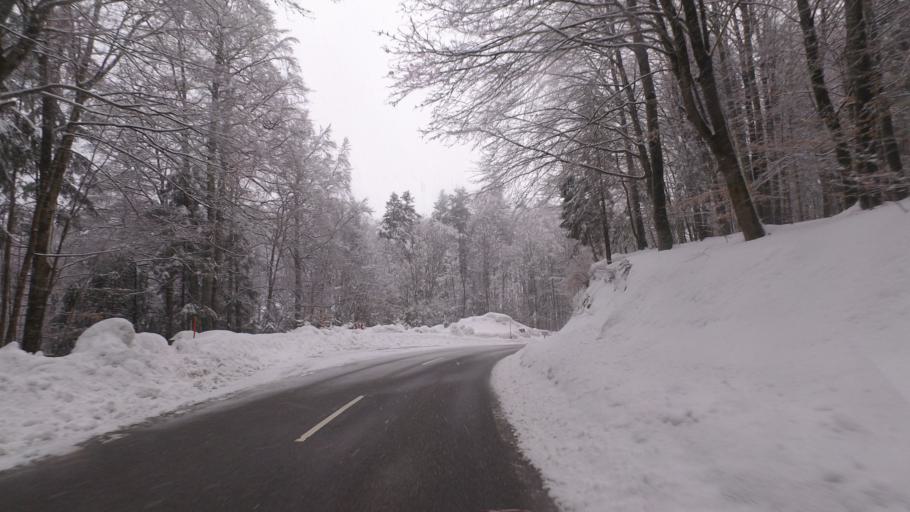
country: DE
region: Bavaria
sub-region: Upper Bavaria
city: Schleching
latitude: 47.6989
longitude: 12.3917
